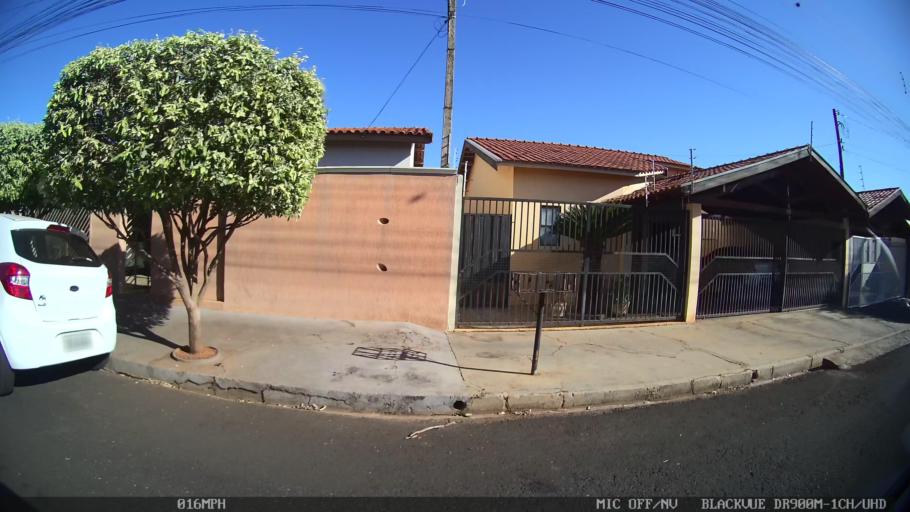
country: BR
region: Sao Paulo
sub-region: Olimpia
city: Olimpia
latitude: -20.7417
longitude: -48.8936
